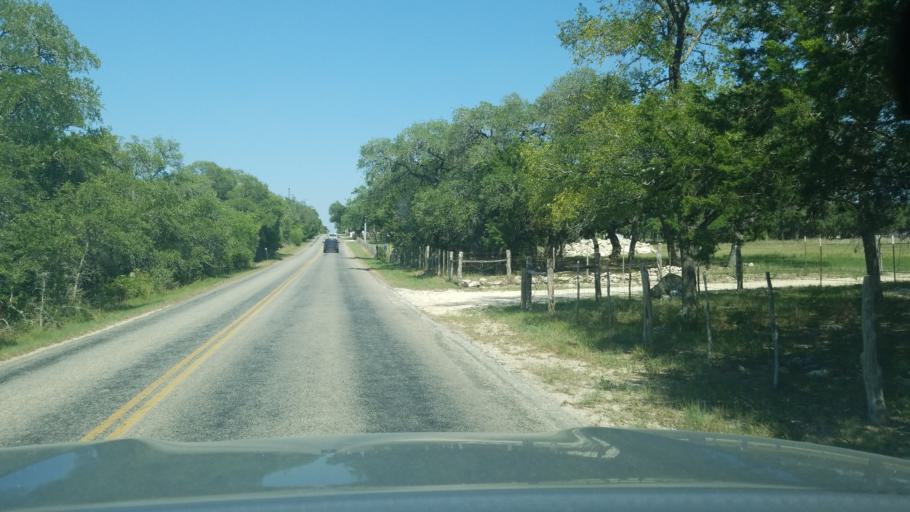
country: US
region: Texas
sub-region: Bexar County
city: Fair Oaks Ranch
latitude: 29.7856
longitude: -98.6433
